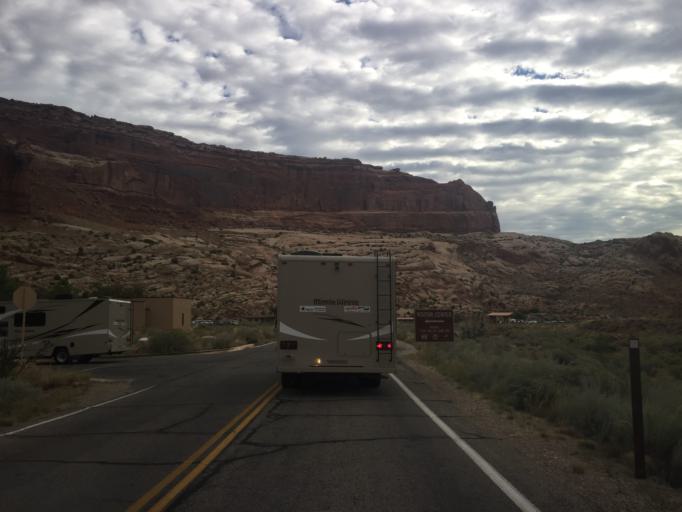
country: US
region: Utah
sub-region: Grand County
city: Moab
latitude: 38.6158
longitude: -109.6203
